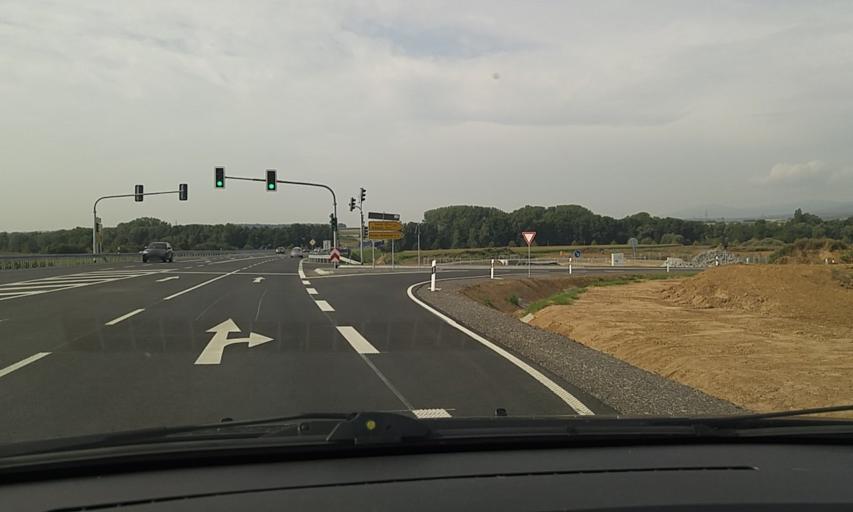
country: DE
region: Hesse
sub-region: Regierungsbezirk Darmstadt
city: Friedberg
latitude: 50.2928
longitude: 8.7662
